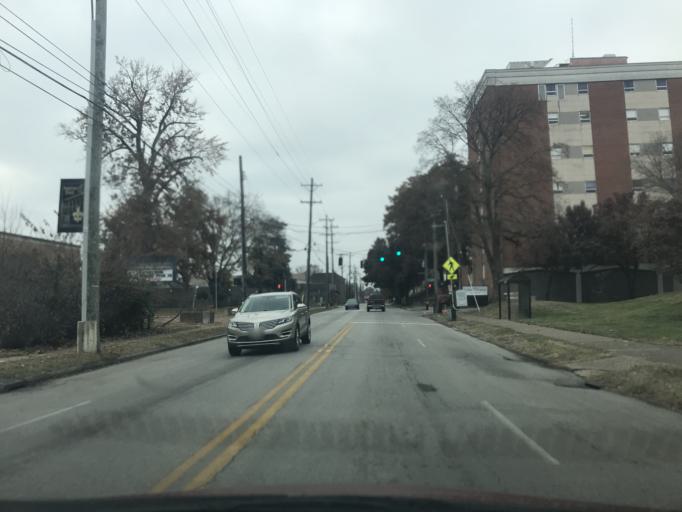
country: US
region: Kentucky
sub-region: Jefferson County
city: Louisville
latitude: 38.2413
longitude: -85.7319
